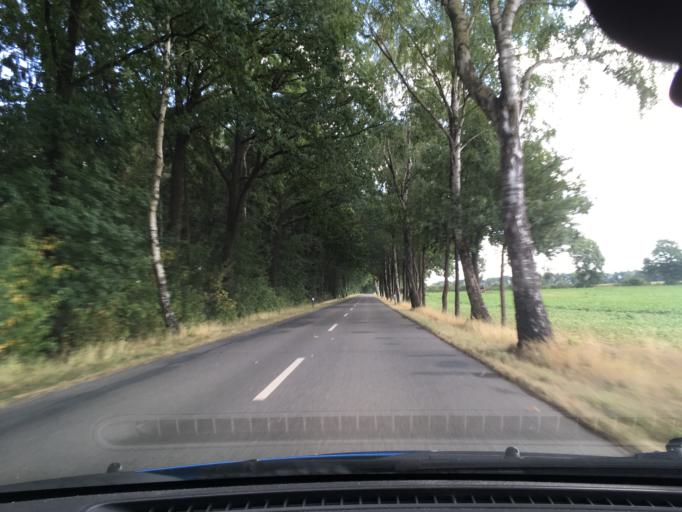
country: DE
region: Lower Saxony
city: Wriedel
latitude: 53.0432
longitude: 10.2655
